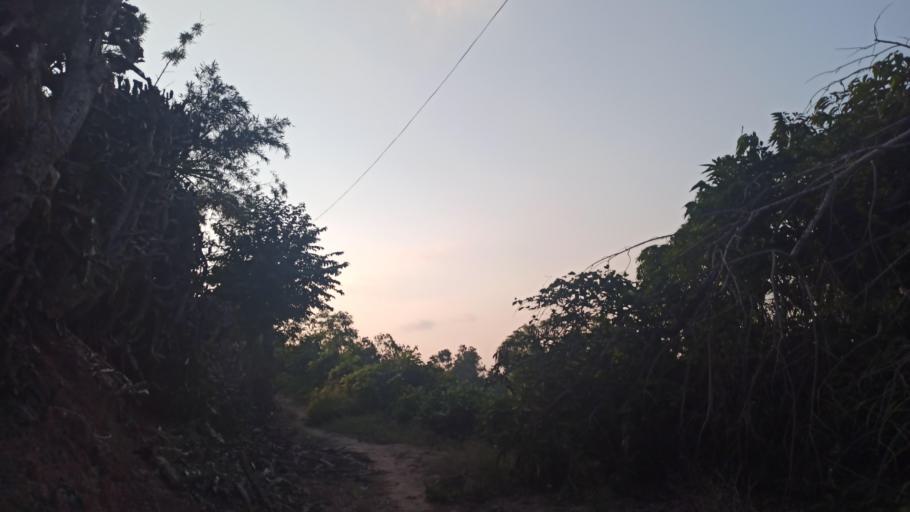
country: MX
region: Veracruz
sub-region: Papantla
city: Polutla
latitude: 20.5937
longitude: -97.2552
